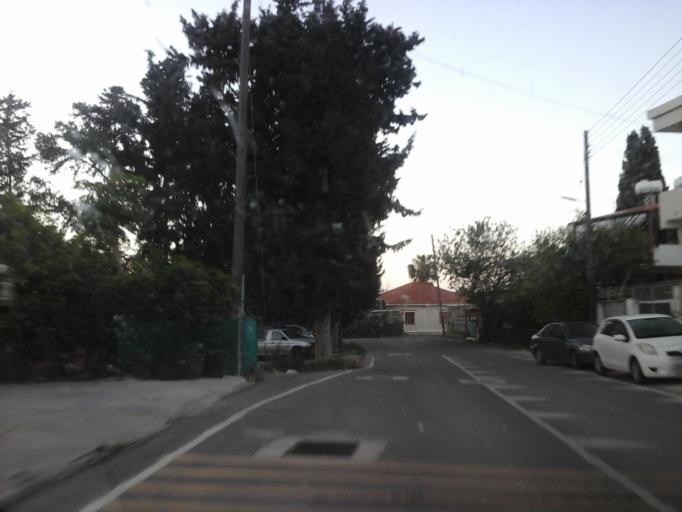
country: CY
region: Pafos
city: Paphos
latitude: 34.7600
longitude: 32.4562
